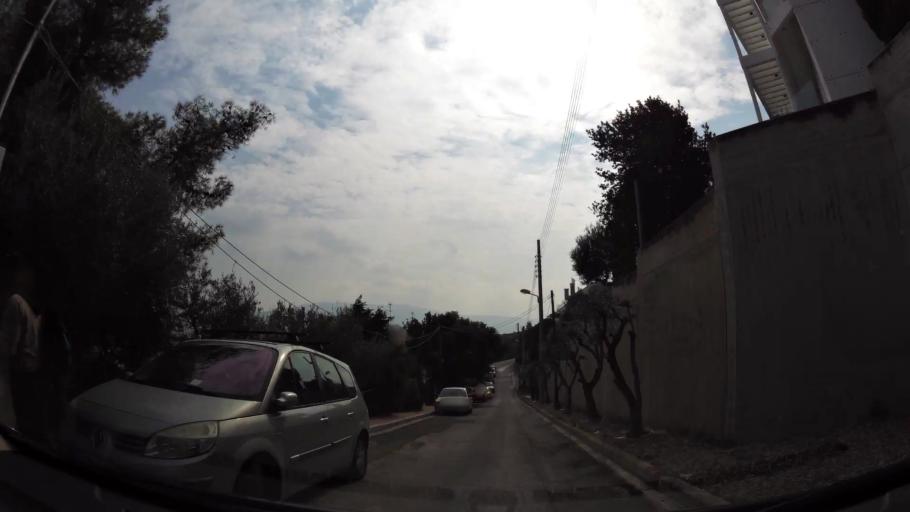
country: GR
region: Attica
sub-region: Nomarchia Athinas
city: Psychiko
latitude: 38.0124
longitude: 23.7649
